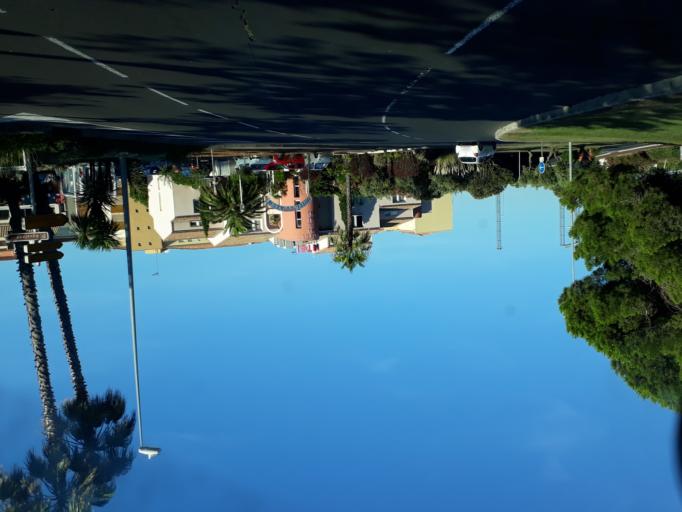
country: FR
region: Languedoc-Roussillon
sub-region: Departement de l'Herault
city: Le Cap d'Agde
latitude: 43.2826
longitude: 3.4978
